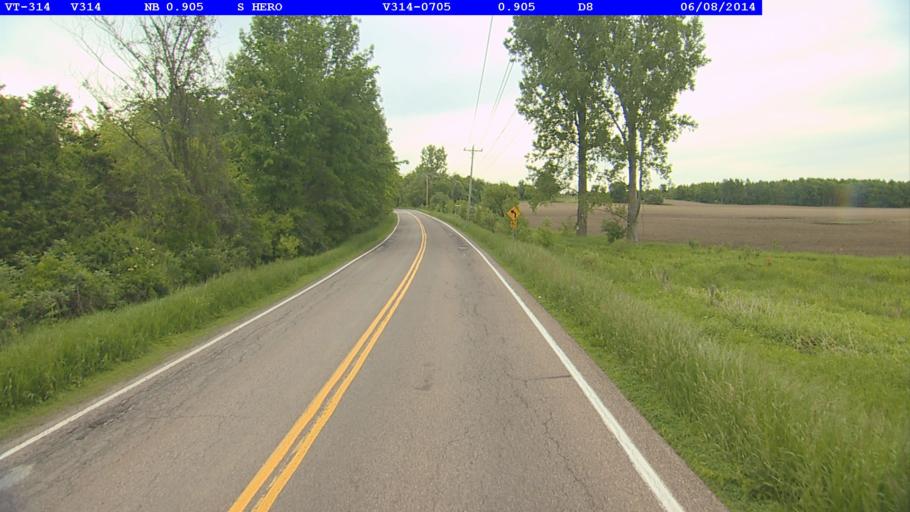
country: US
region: New York
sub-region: Clinton County
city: Cumberland Head
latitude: 44.6714
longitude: -73.3368
